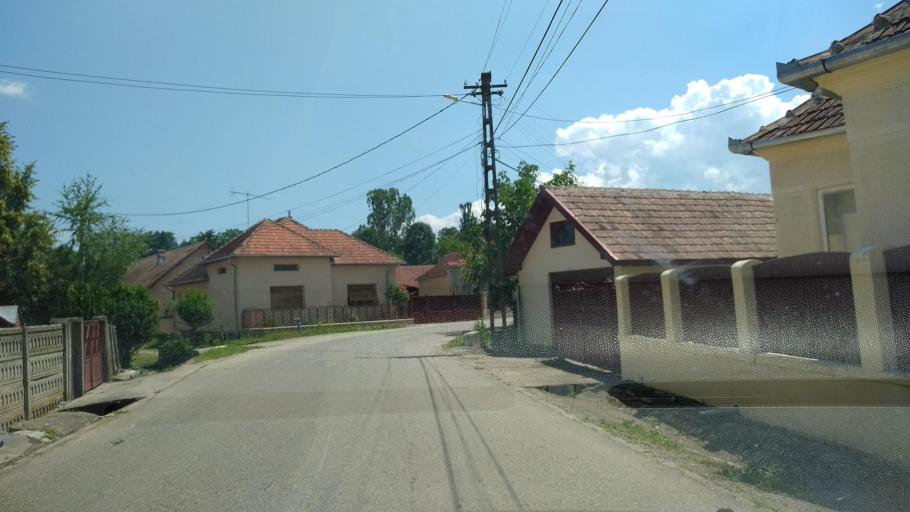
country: RO
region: Hunedoara
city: Densus
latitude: 45.5553
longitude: 22.8213
